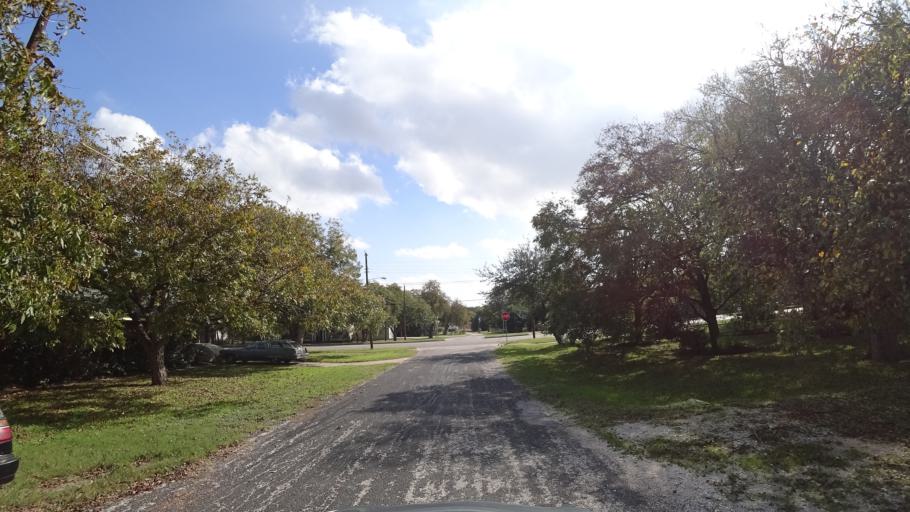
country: US
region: Texas
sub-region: Williamson County
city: Round Rock
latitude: 30.5104
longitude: -97.6737
